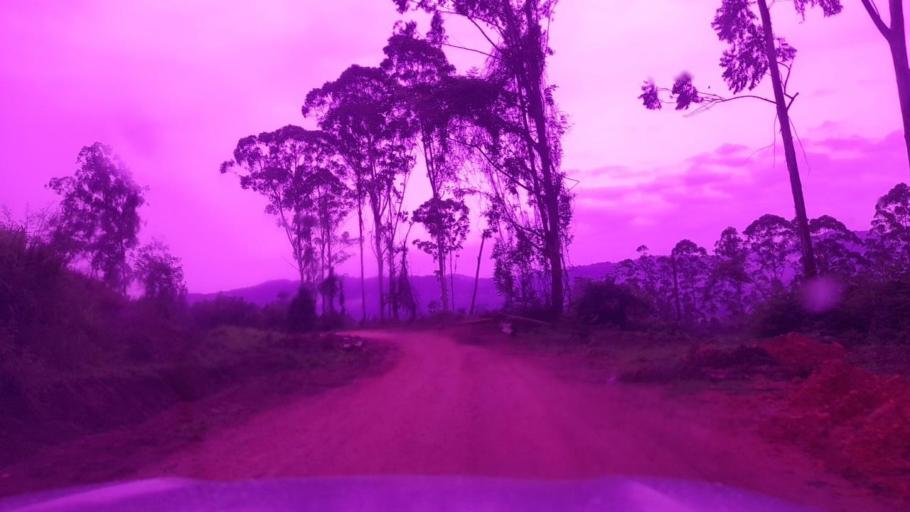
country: ET
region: Southern Nations, Nationalities, and People's Region
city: Bonga
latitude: 7.4495
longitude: 36.1457
